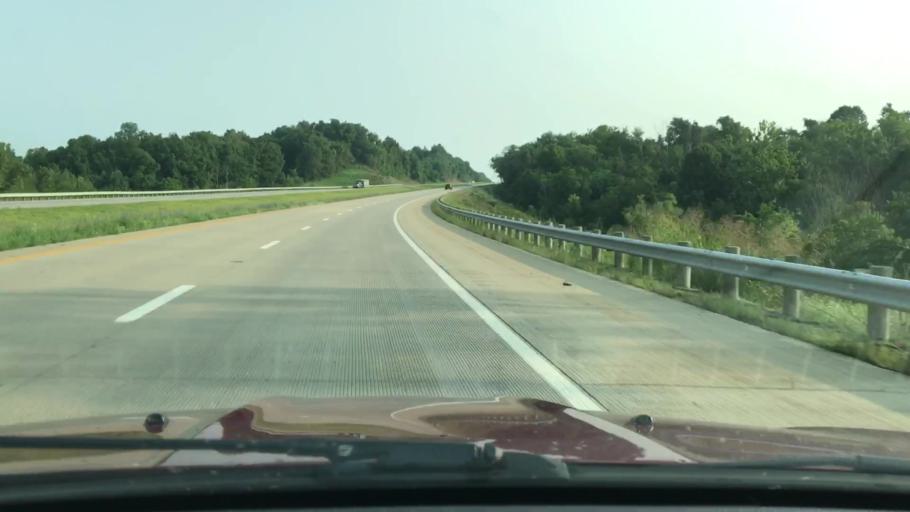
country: US
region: Ohio
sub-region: Washington County
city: Devola
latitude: 39.5911
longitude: -81.4613
